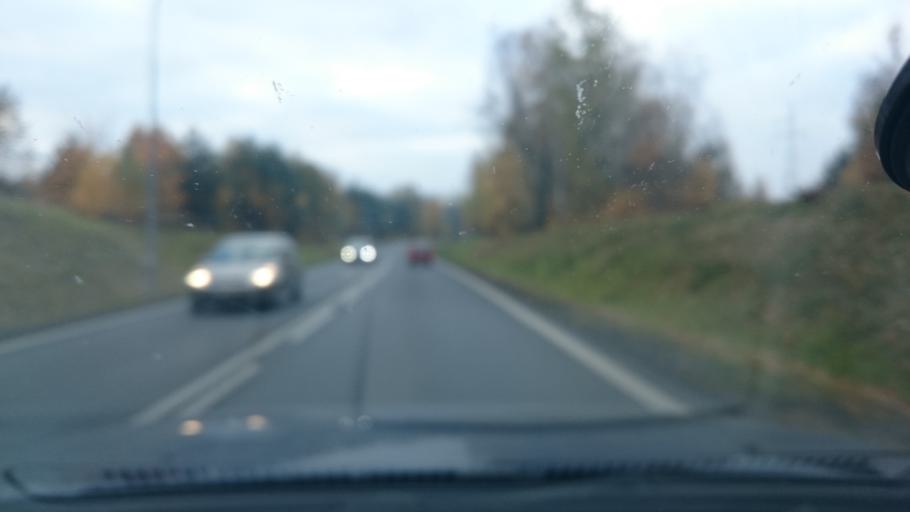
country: PL
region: Silesian Voivodeship
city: Zebrzydowice
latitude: 50.1079
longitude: 18.5161
